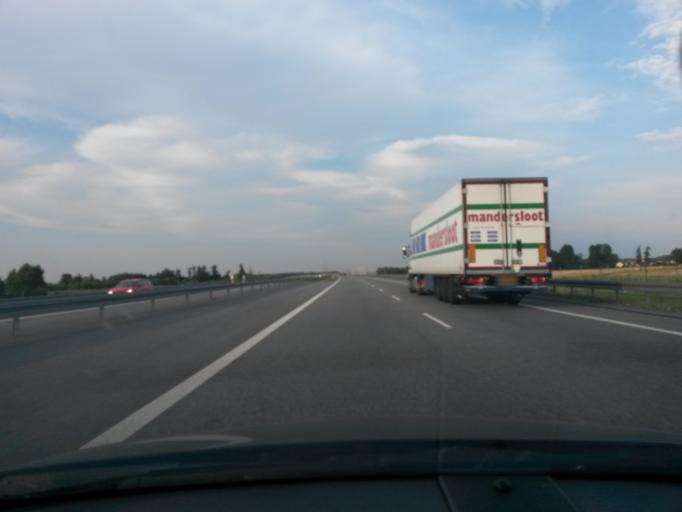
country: PL
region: Lodz Voivodeship
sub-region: powiat Lowicki
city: Lyszkowice
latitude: 52.0071
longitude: 19.9530
